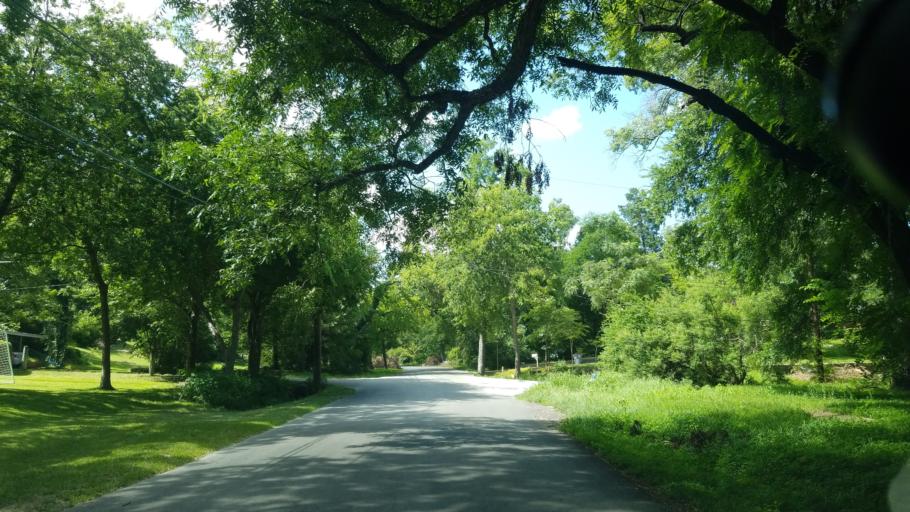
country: US
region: Texas
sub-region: Dallas County
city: Balch Springs
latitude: 32.7662
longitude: -96.6953
